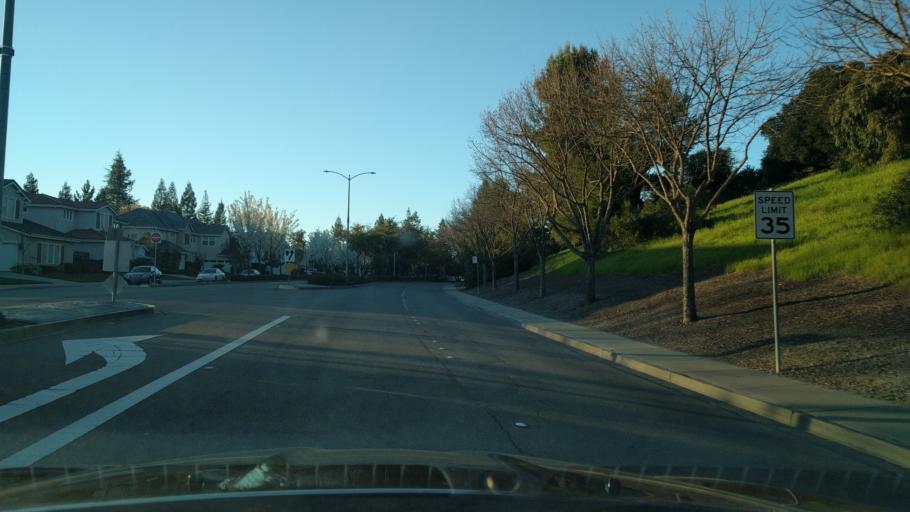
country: US
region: California
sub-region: Contra Costa County
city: San Ramon
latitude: 37.7543
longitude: -121.9391
